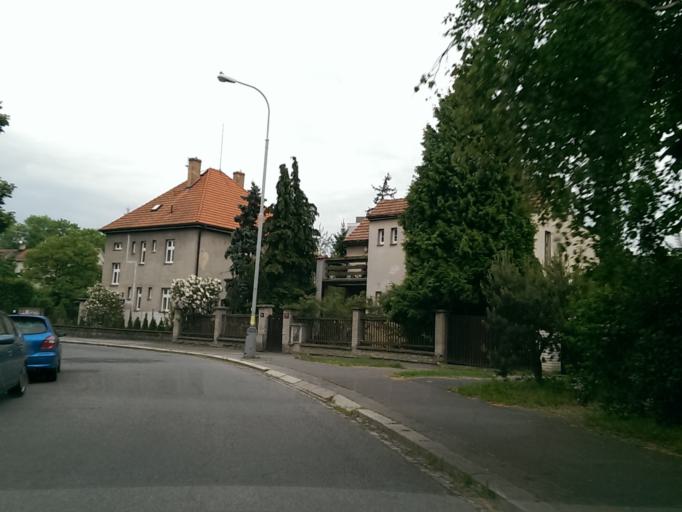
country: CZ
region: Praha
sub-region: Praha 8
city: Karlin
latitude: 50.0485
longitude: 14.4628
